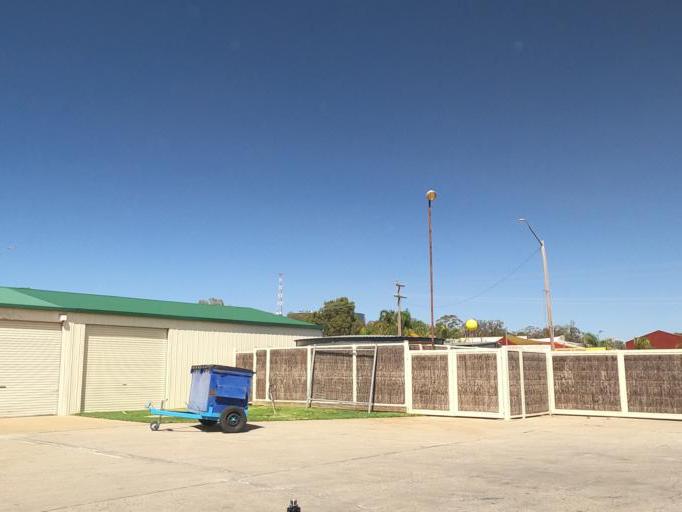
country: AU
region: New South Wales
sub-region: Corowa Shire
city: Mulwala
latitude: -35.9955
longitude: 146.0015
